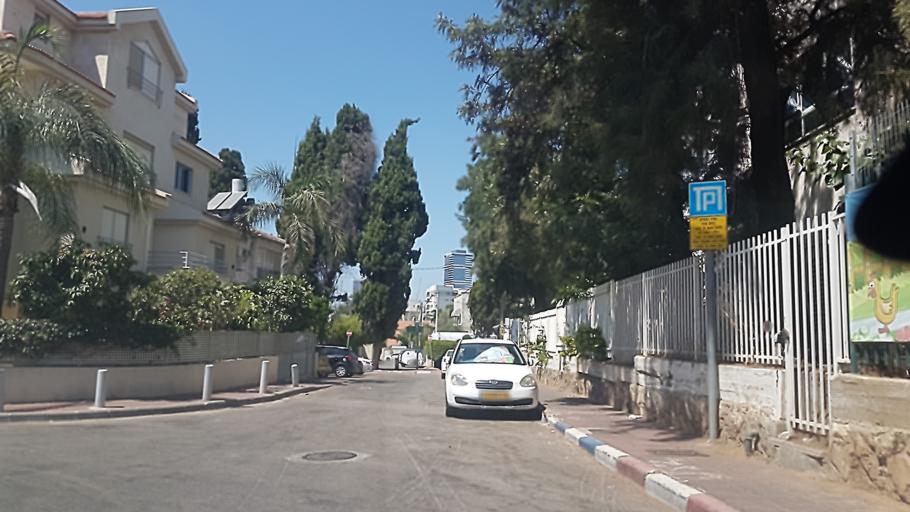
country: IL
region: Tel Aviv
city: Bene Beraq
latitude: 32.0810
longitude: 34.8230
